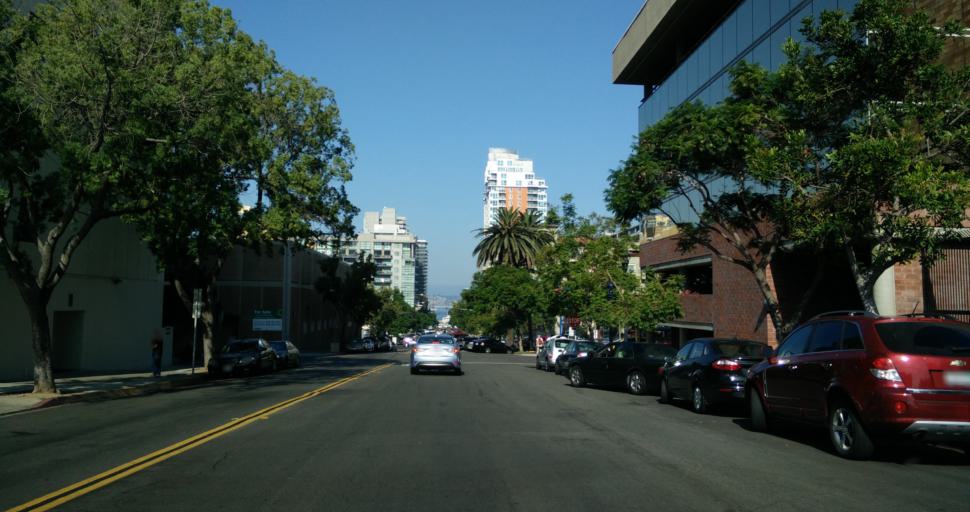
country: US
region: California
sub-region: San Diego County
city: San Diego
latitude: 32.7209
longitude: -117.1623
